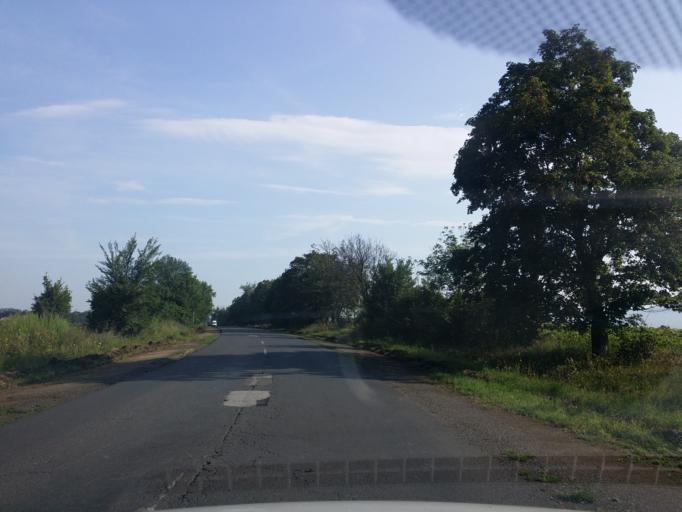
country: HU
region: Borsod-Abauj-Zemplen
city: Abaujszanto
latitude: 48.3560
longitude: 21.2149
